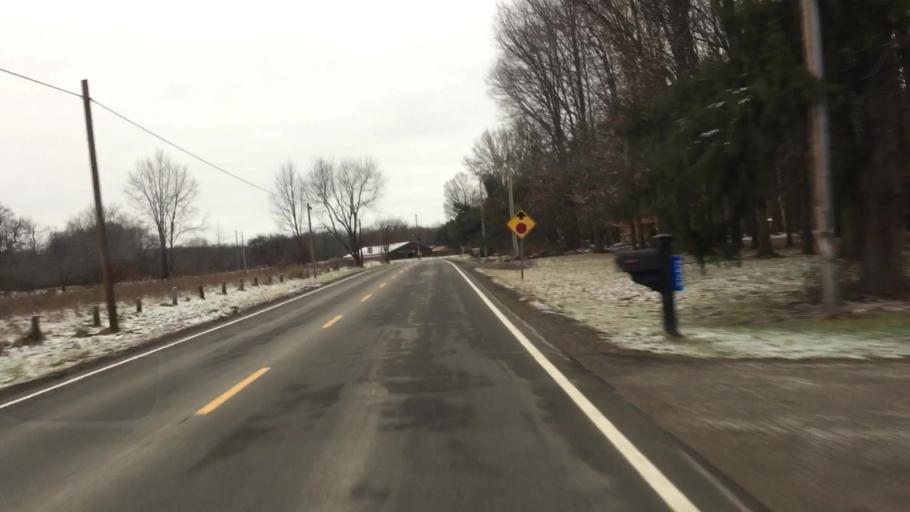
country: US
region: Ohio
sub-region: Summit County
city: Norton
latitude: 41.0737
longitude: -81.6366
